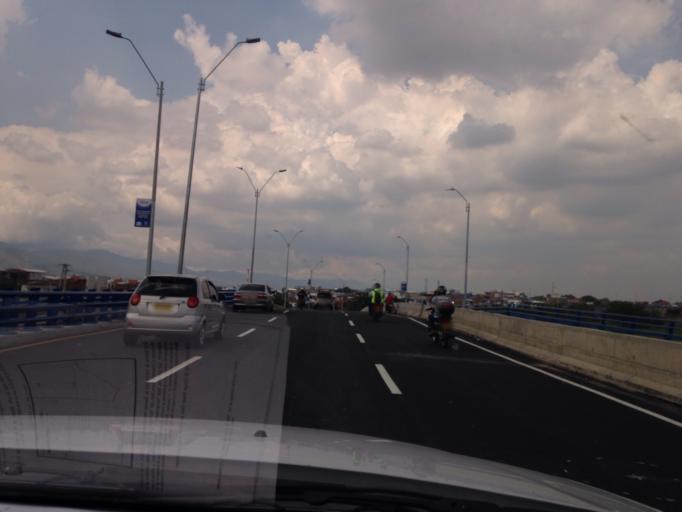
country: CO
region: Valle del Cauca
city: Cali
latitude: 3.3891
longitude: -76.5163
